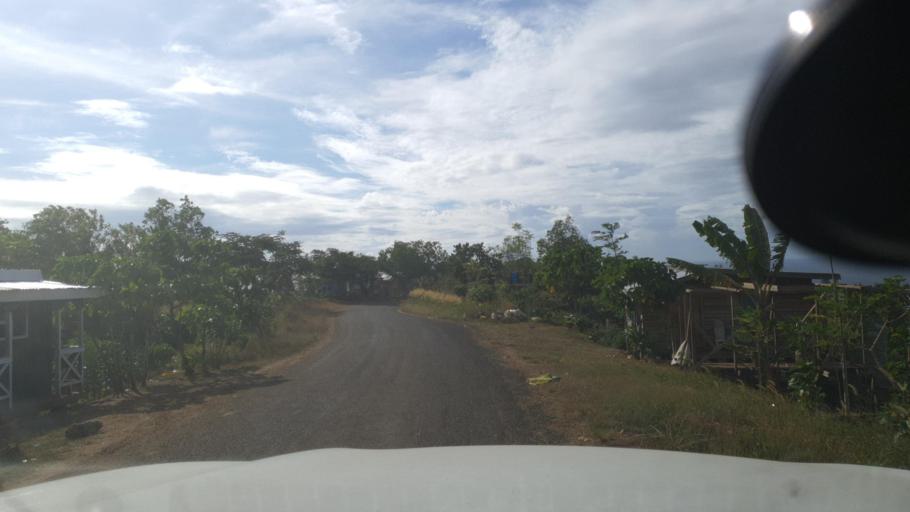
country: SB
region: Guadalcanal
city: Honiara
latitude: -9.4433
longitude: 159.9375
